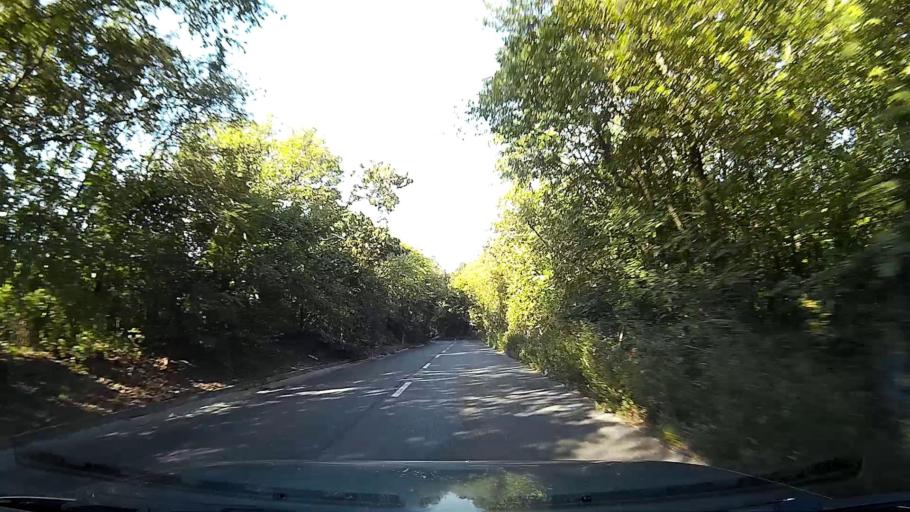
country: HU
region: Pest
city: Diosd
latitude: 47.4282
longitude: 18.9802
